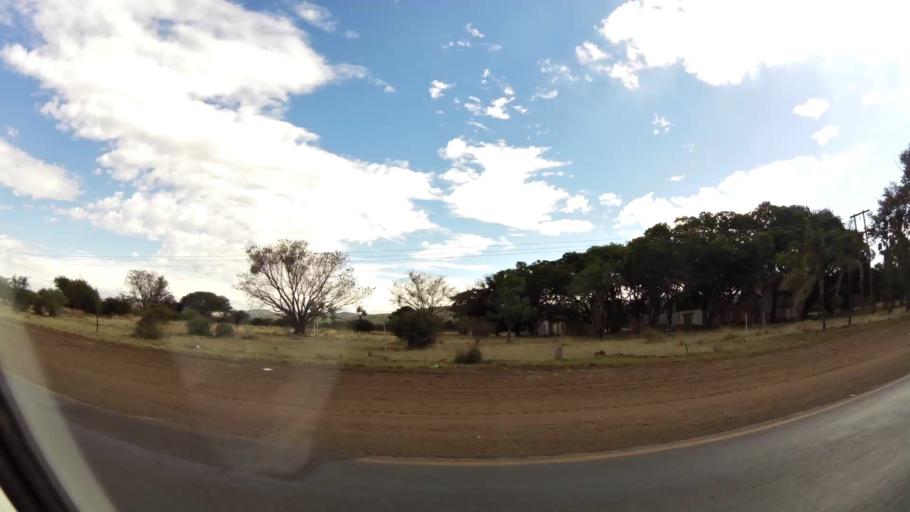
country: ZA
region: Limpopo
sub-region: Waterberg District Municipality
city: Bela-Bela
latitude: -24.8688
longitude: 28.3229
